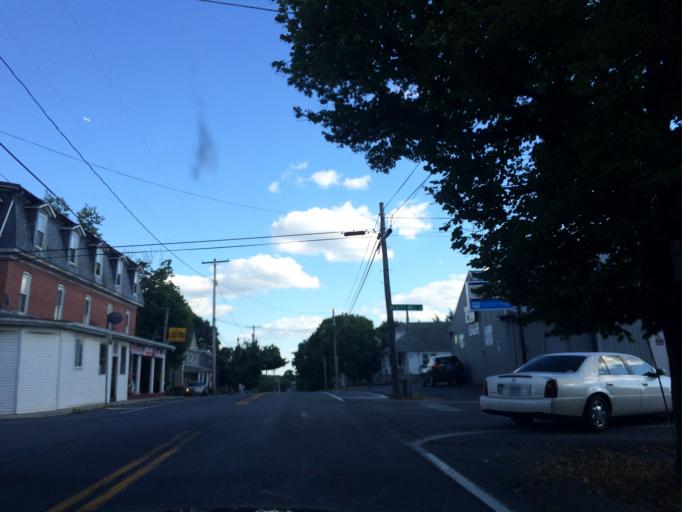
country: US
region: Maryland
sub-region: Frederick County
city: Thurmont
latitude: 39.5772
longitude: -77.3652
